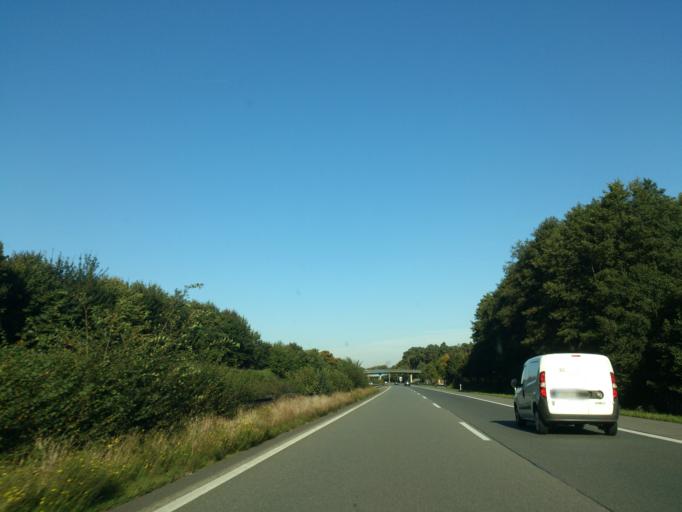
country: DE
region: North Rhine-Westphalia
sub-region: Regierungsbezirk Detmold
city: Verl
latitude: 51.9333
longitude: 8.5729
